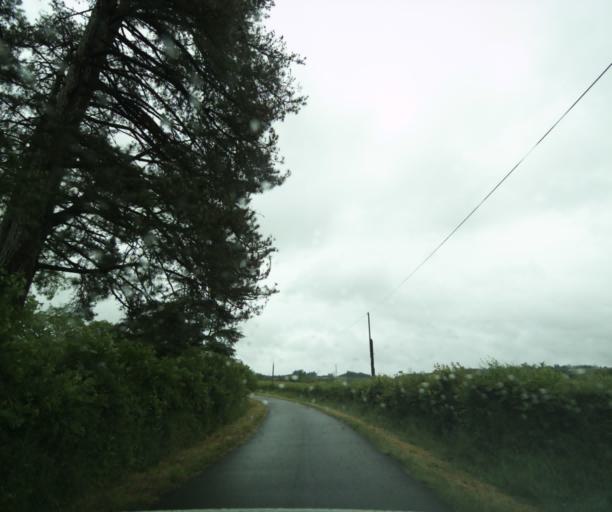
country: FR
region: Bourgogne
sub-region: Departement de Saone-et-Loire
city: Saint-Vallier
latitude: 46.4938
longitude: 4.4591
